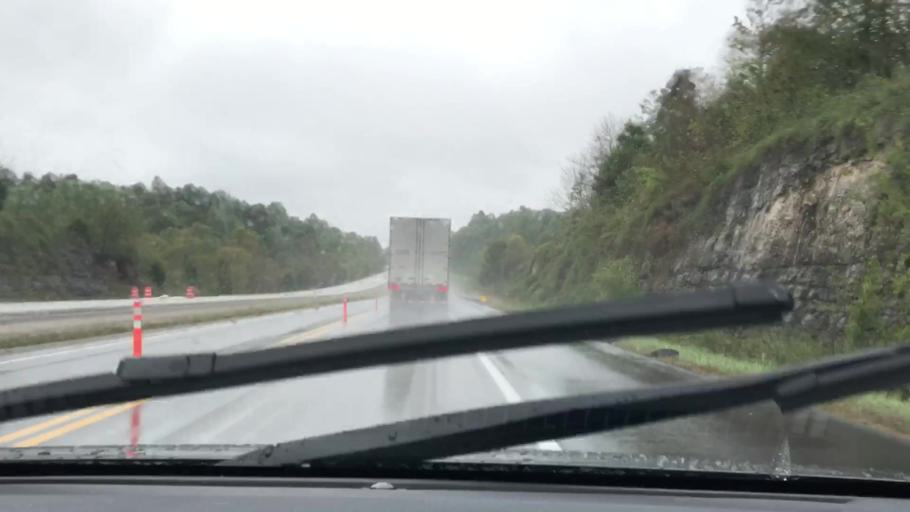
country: US
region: Kentucky
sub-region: Christian County
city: Hopkinsville
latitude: 37.0023
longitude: -87.4628
